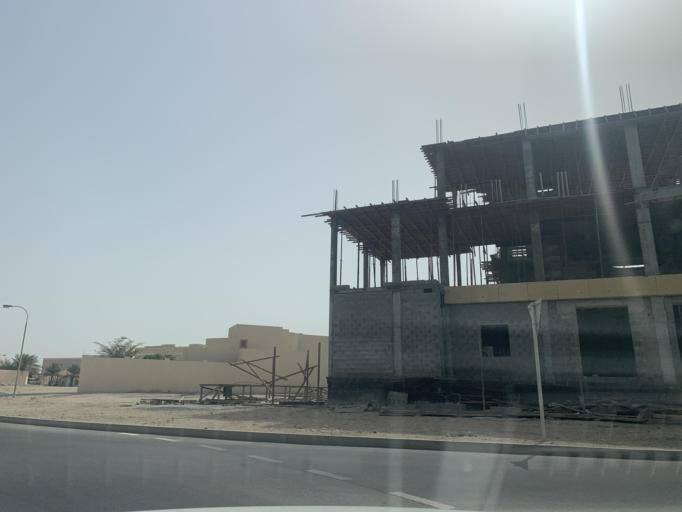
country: BH
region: Central Governorate
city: Madinat Hamad
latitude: 26.1438
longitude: 50.5150
